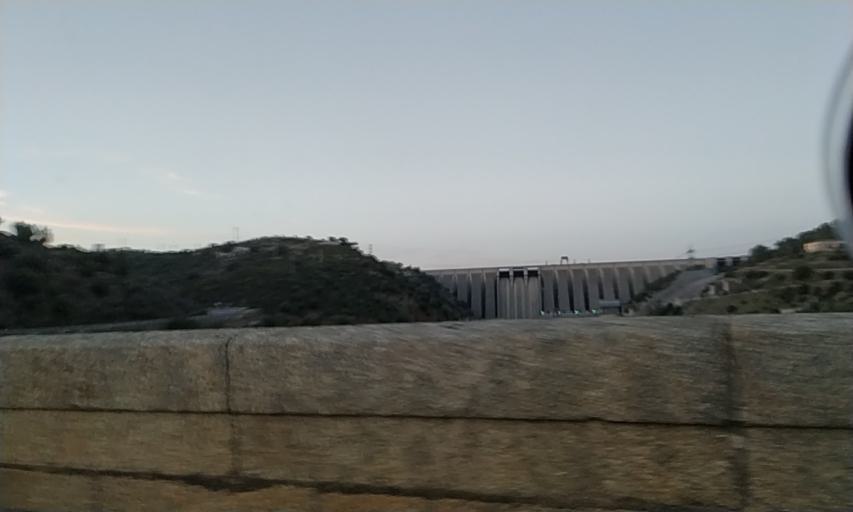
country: ES
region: Extremadura
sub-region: Provincia de Caceres
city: Alcantara
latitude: 39.7222
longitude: -6.8922
